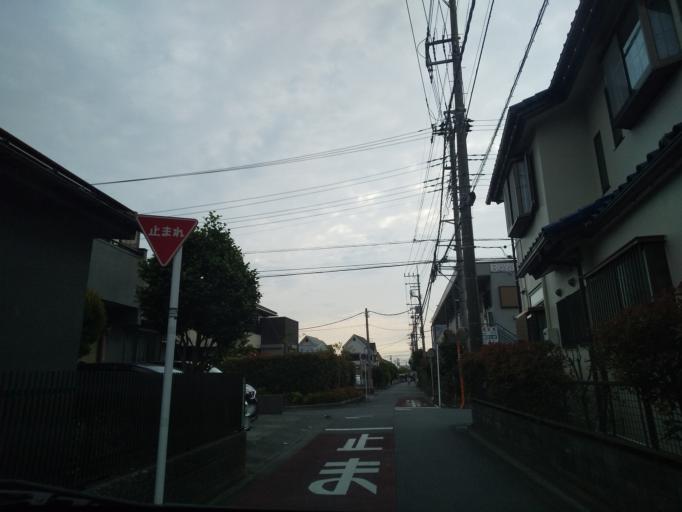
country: JP
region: Tokyo
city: Hachioji
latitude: 35.5952
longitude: 139.3596
